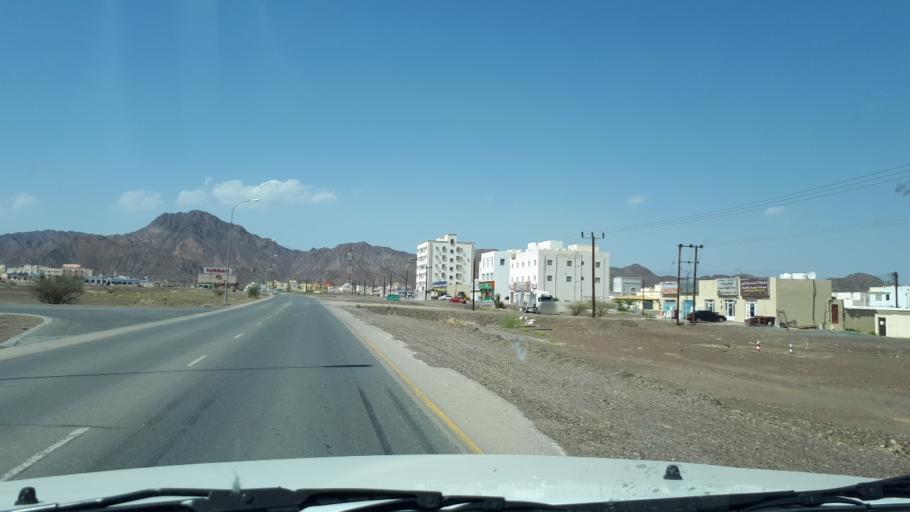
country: OM
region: Muhafazat ad Dakhiliyah
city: Bahla'
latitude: 22.9425
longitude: 57.2595
